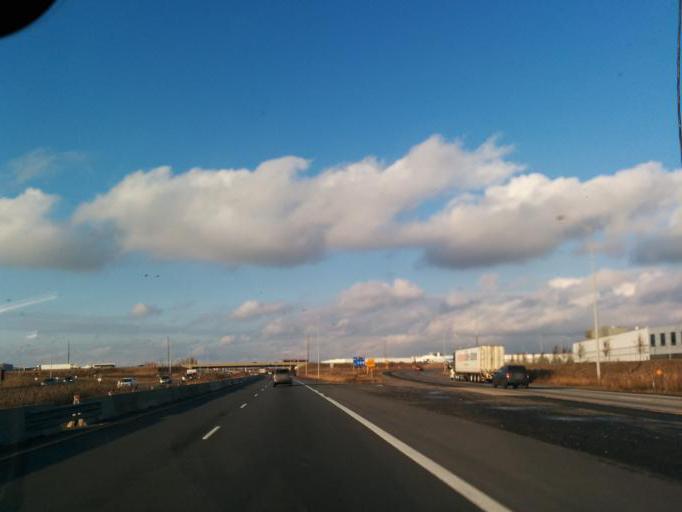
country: CA
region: Ontario
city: Etobicoke
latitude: 43.7666
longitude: -79.6332
